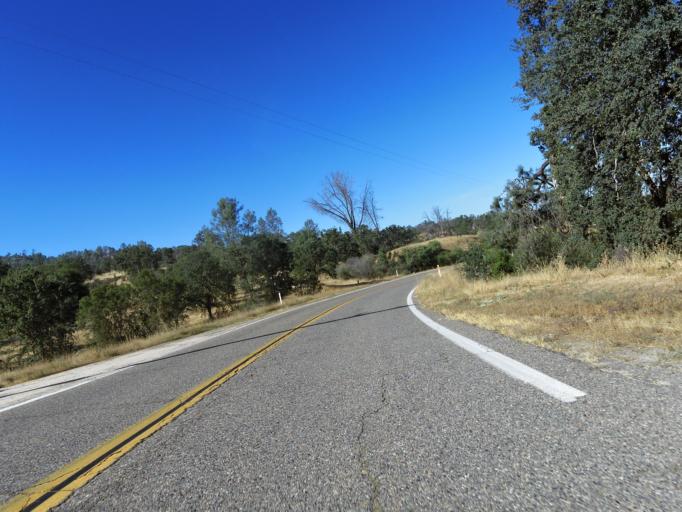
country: US
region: California
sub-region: Madera County
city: Yosemite Lakes
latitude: 37.1970
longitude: -119.8004
